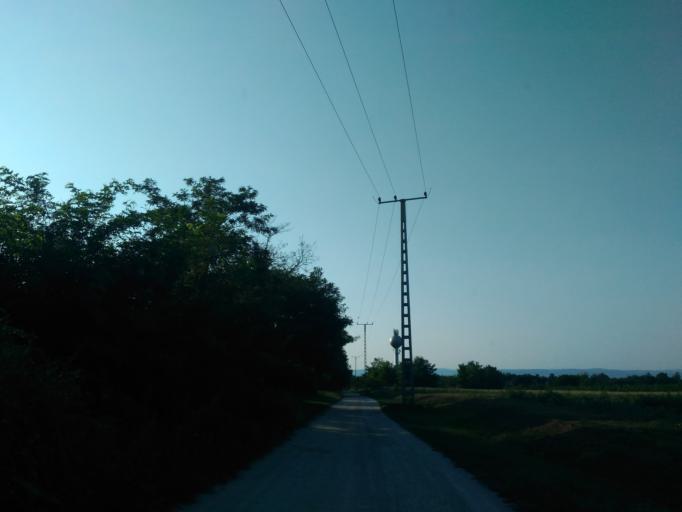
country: HU
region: Somogy
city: Balatonszarszo
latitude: 46.7974
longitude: 17.7877
